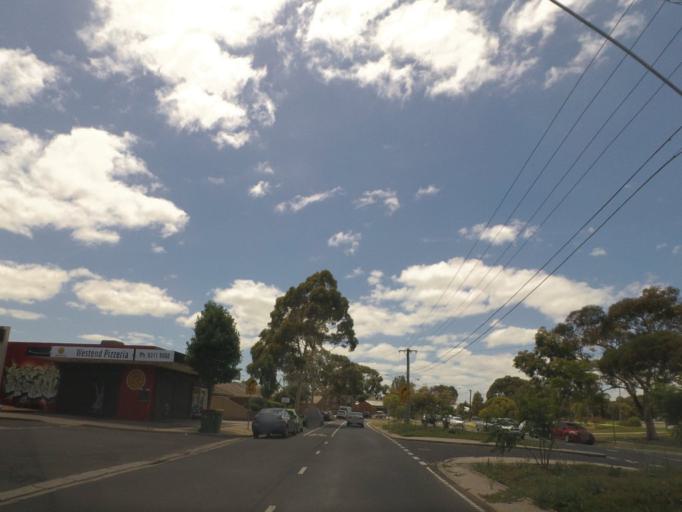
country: AU
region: Victoria
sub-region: Maribyrnong
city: Braybrook
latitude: -37.7859
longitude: 144.8537
